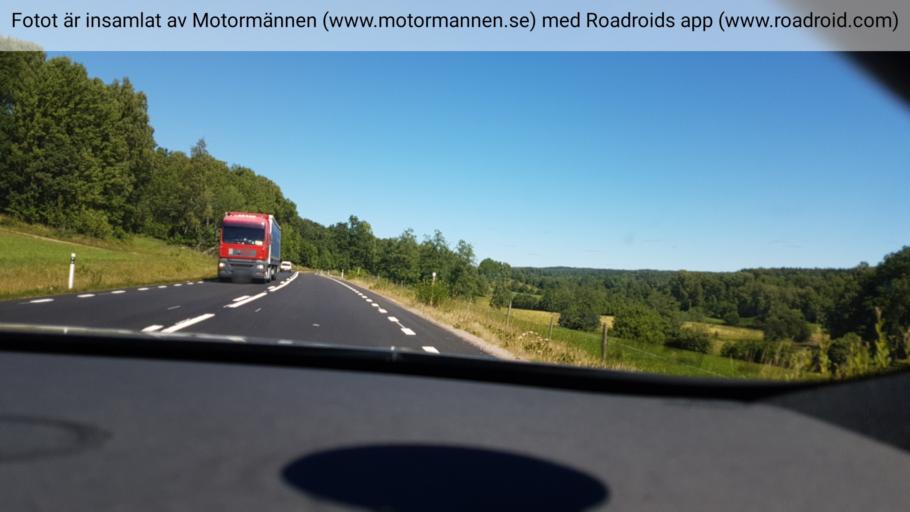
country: SE
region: Vaestra Goetaland
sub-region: Ulricehamns Kommun
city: Ulricehamn
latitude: 57.9076
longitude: 13.4750
